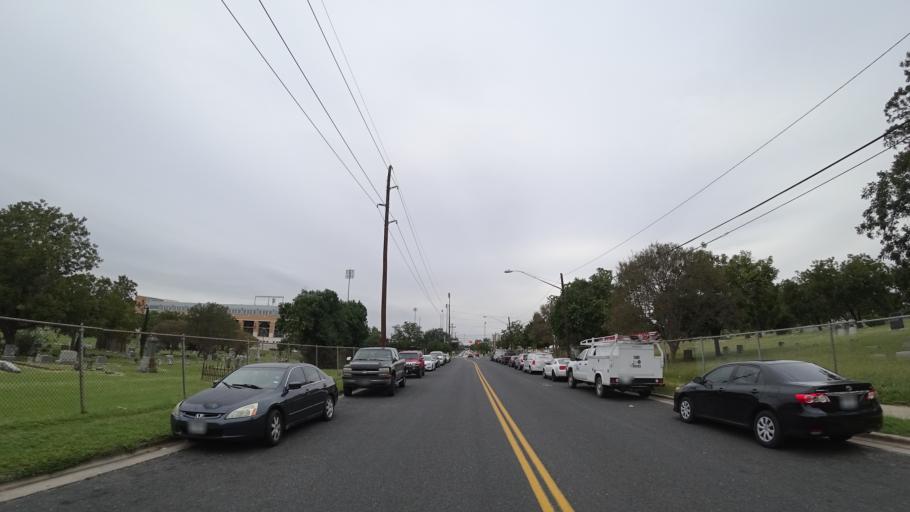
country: US
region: Texas
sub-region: Travis County
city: Austin
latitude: 30.2779
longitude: -97.7249
